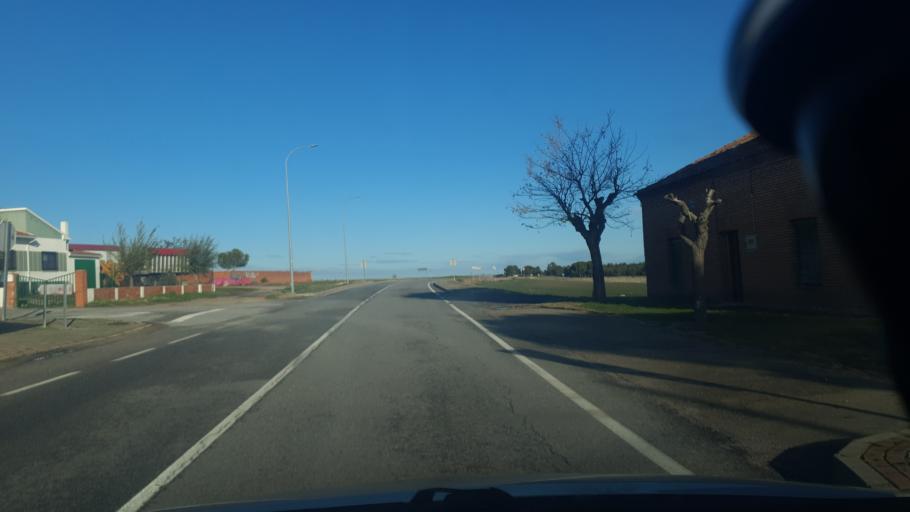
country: ES
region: Castille and Leon
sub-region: Provincia de Avila
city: Tinosillos
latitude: 40.9162
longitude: -4.7287
